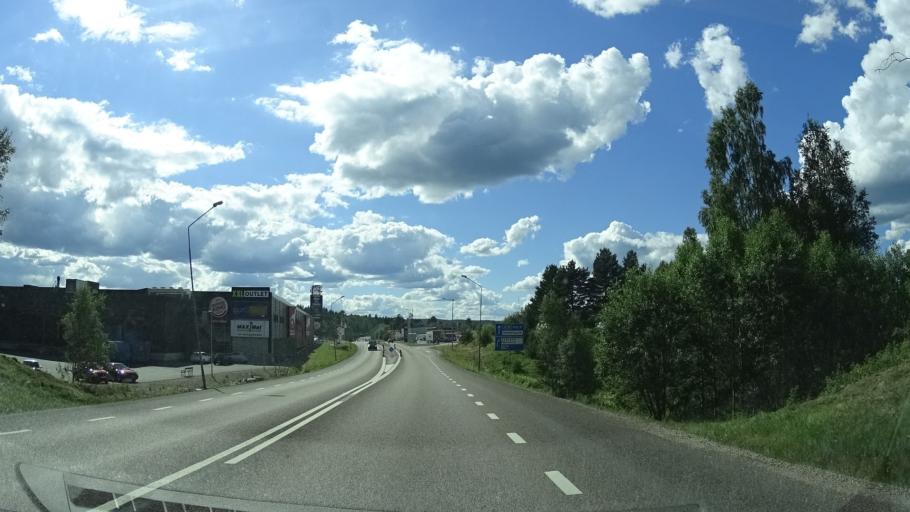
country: SE
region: Vaermland
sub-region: Arjangs Kommun
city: Toecksfors
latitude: 59.5077
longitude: 11.8479
